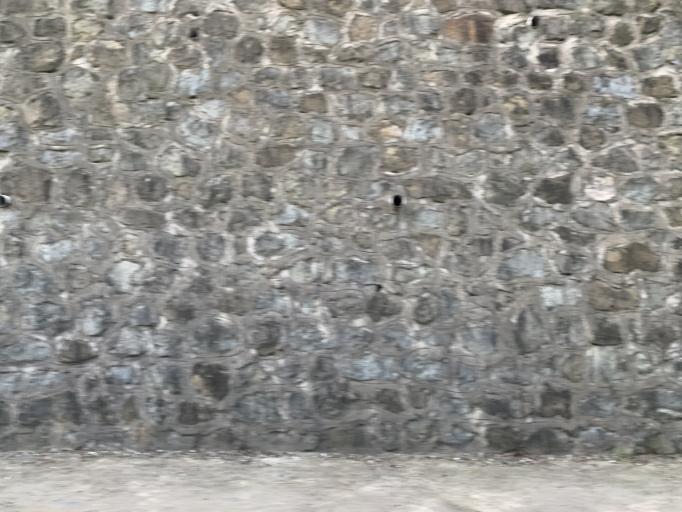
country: TR
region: Trabzon
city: Dernekpazari
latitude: 40.8307
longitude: 40.2692
